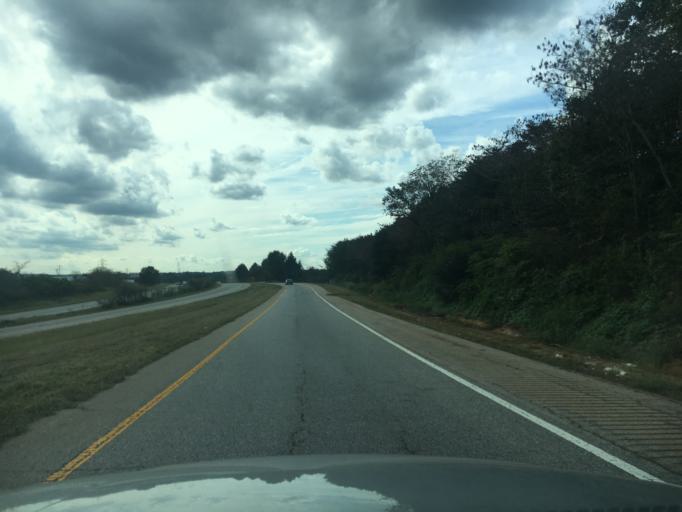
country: US
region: South Carolina
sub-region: Spartanburg County
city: Fairforest
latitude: 34.9652
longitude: -82.0330
